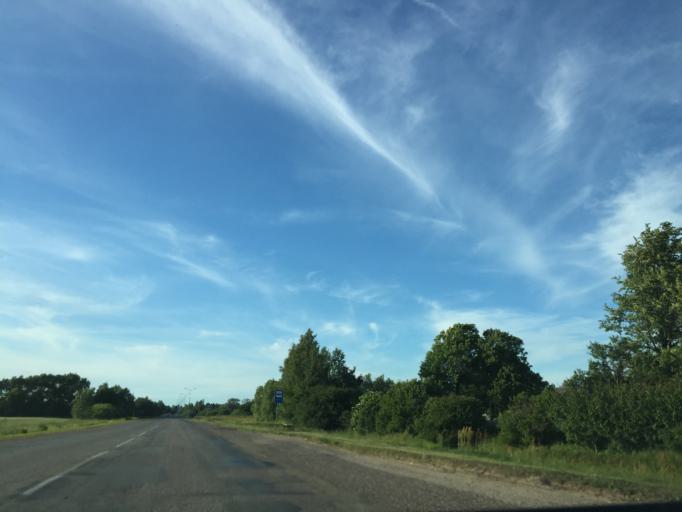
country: LV
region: Ventspils
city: Ventspils
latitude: 57.3524
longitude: 21.5643
